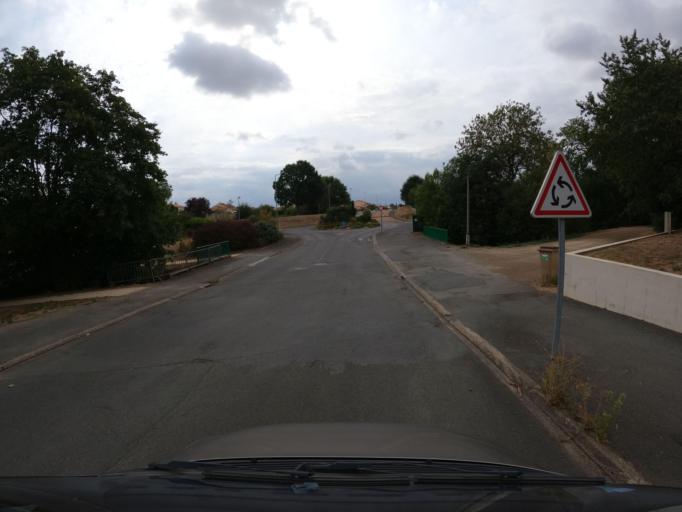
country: FR
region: Pays de la Loire
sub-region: Departement de Maine-et-Loire
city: Saint-Christophe-du-Bois
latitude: 47.0335
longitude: -0.9427
